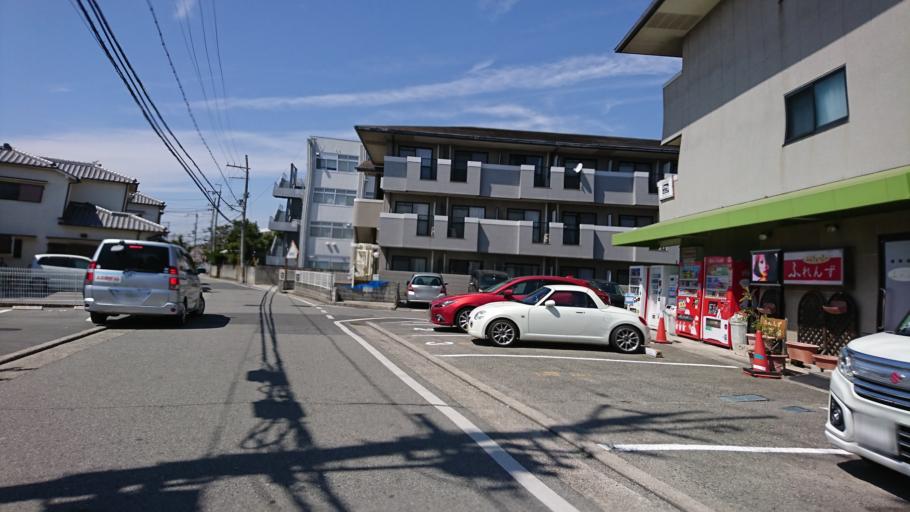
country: JP
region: Hyogo
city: Kakogawacho-honmachi
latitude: 34.7459
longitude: 134.8832
